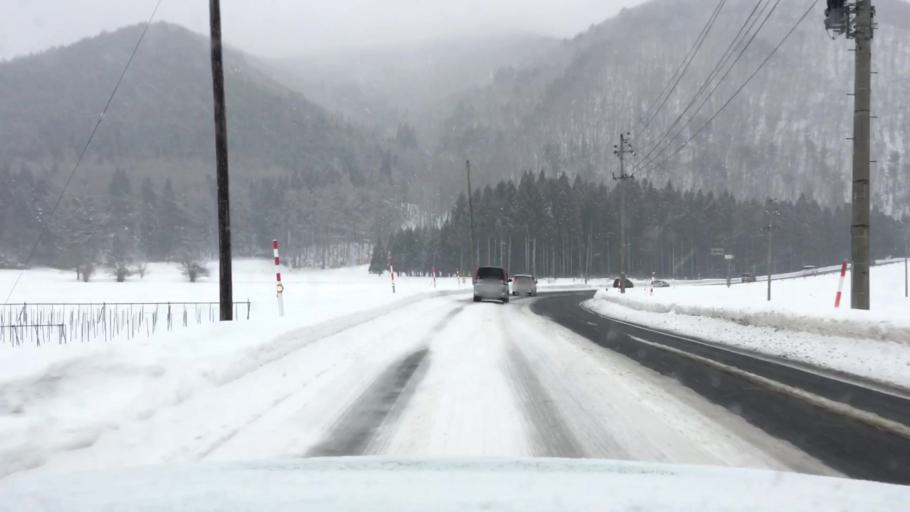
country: JP
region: Akita
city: Hanawa
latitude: 40.0798
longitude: 141.0231
